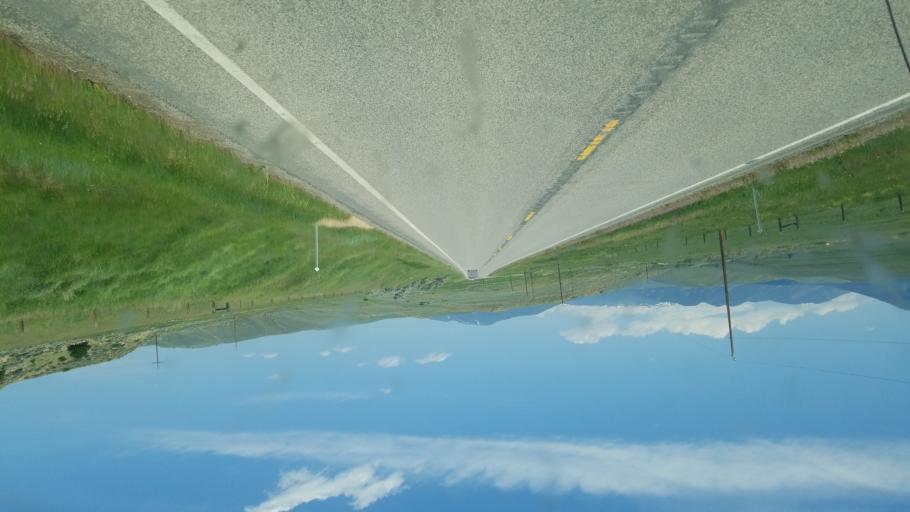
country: US
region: Montana
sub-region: Carbon County
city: Red Lodge
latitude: 45.1656
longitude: -109.1049
